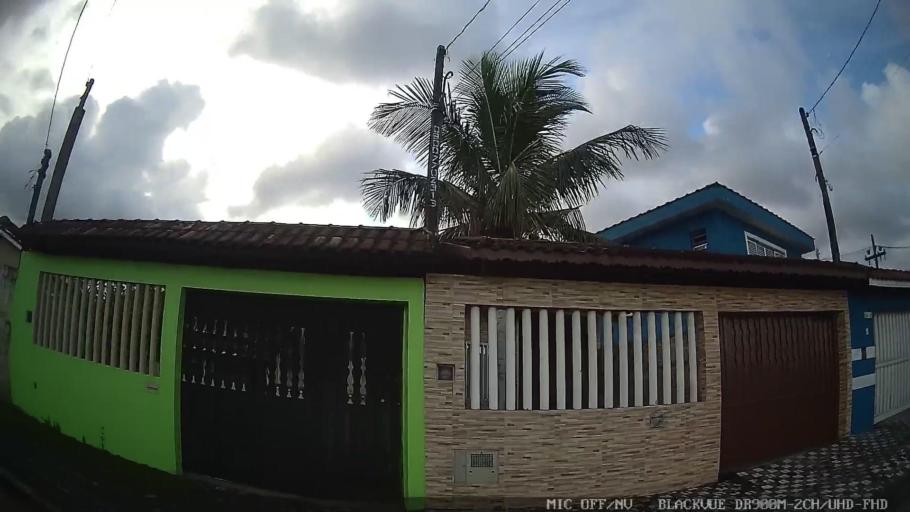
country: BR
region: Sao Paulo
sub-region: Mongagua
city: Mongagua
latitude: -24.1173
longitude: -46.6739
